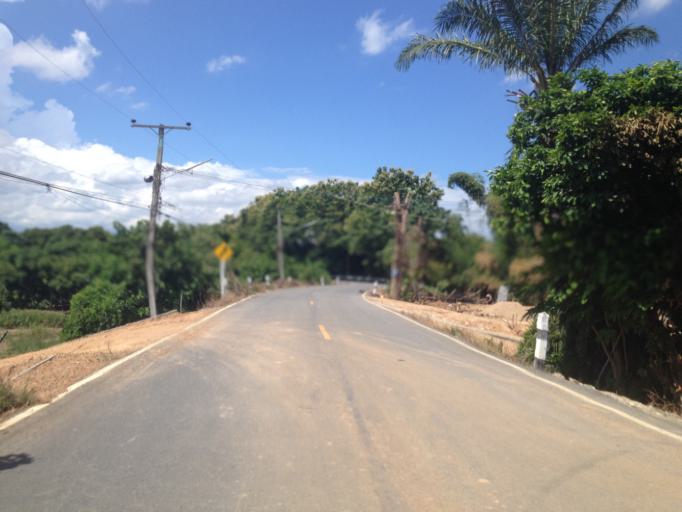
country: TH
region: Chiang Mai
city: San Pa Tong
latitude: 18.6261
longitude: 98.9558
